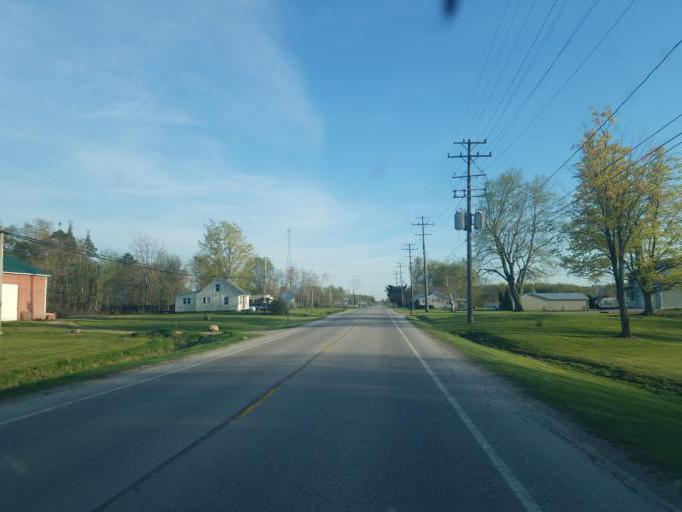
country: US
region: Ohio
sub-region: Ashtabula County
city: Conneaut
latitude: 41.8350
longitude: -80.5721
